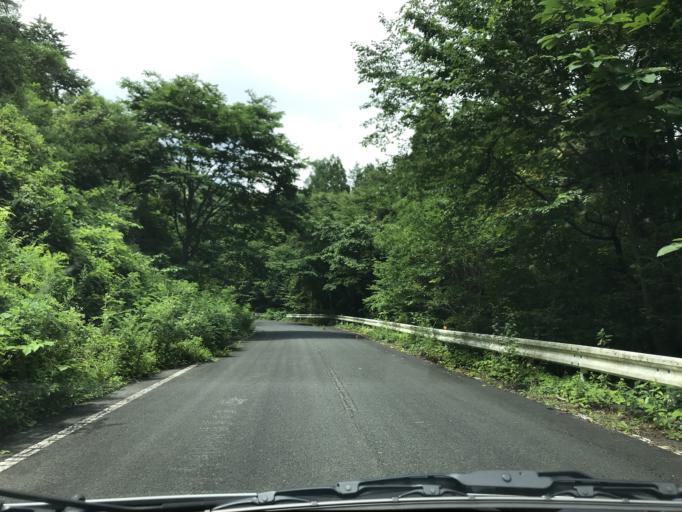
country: JP
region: Iwate
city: Tono
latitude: 39.0909
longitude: 141.4146
